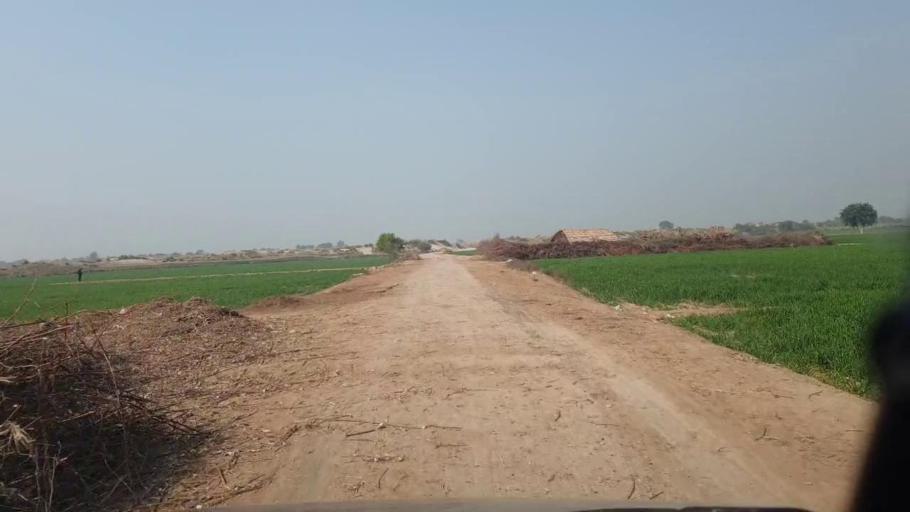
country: PK
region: Sindh
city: Shahdadpur
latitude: 26.0325
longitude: 68.5257
